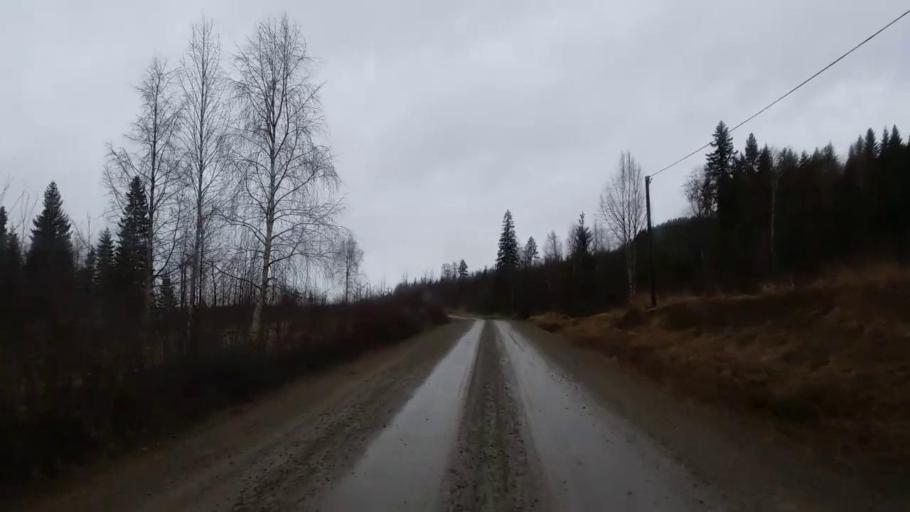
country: SE
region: Gaevleborg
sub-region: Ljusdals Kommun
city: Farila
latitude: 62.0650
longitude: 15.7865
